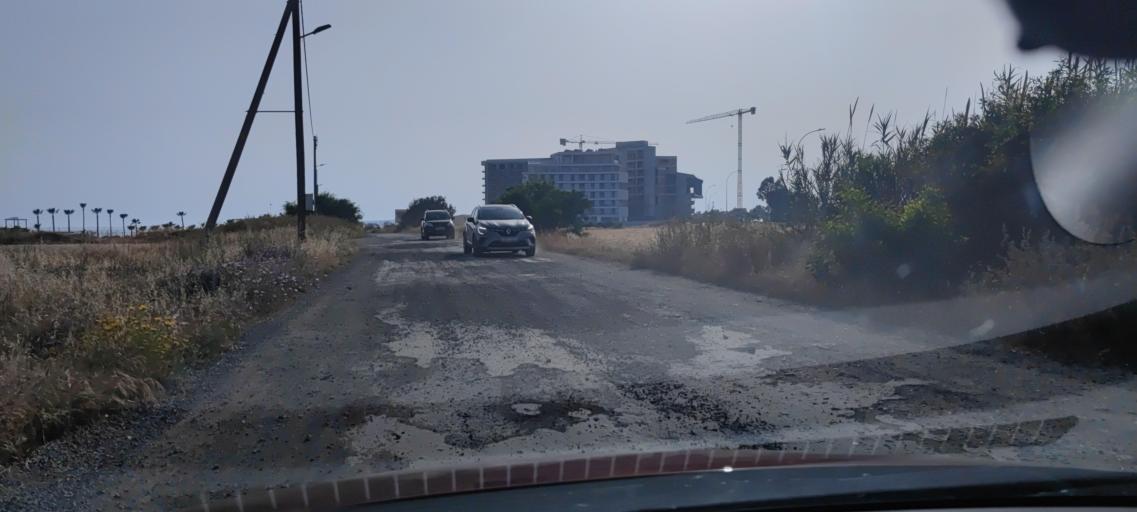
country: CY
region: Ammochostos
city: Liopetri
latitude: 34.9811
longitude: 33.9370
